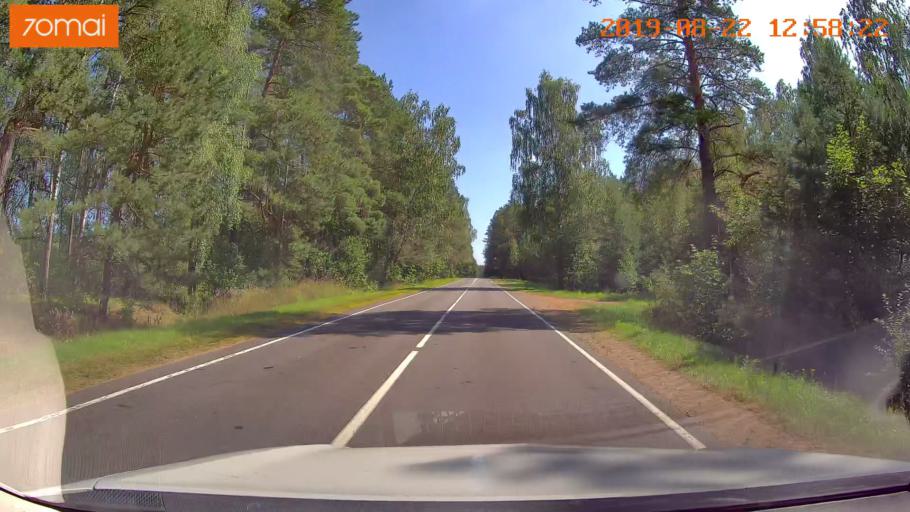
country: BY
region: Minsk
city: Prawdzinski
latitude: 53.4244
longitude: 27.7690
